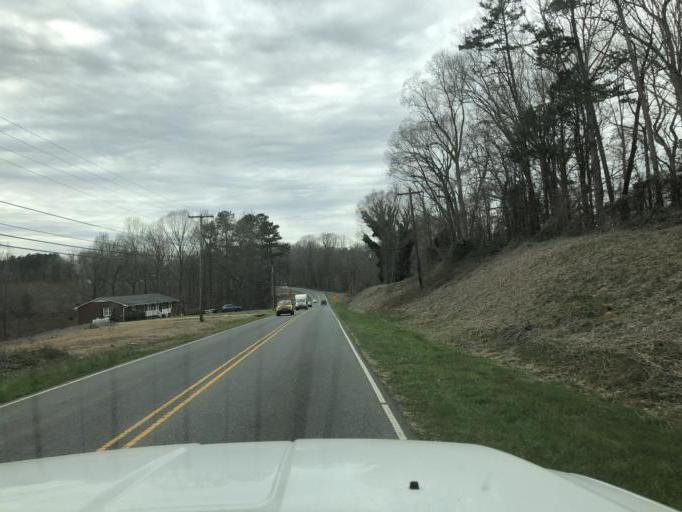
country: US
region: North Carolina
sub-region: Gaston County
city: Dallas
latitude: 35.3220
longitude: -81.1617
